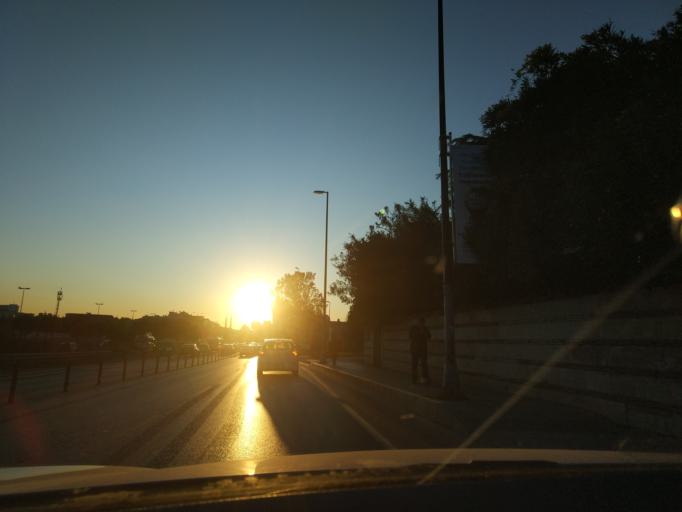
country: TR
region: Istanbul
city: UEskuedar
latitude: 41.0232
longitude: 29.0494
